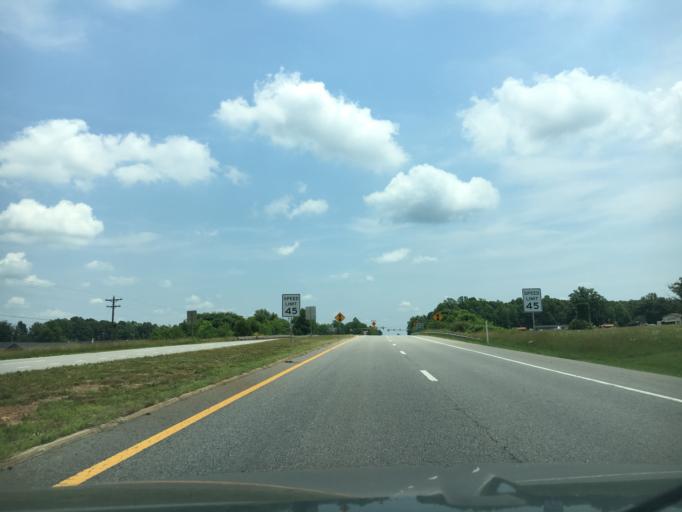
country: US
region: Virginia
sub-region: Buckingham County
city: Buckingham
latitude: 37.5307
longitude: -78.4958
